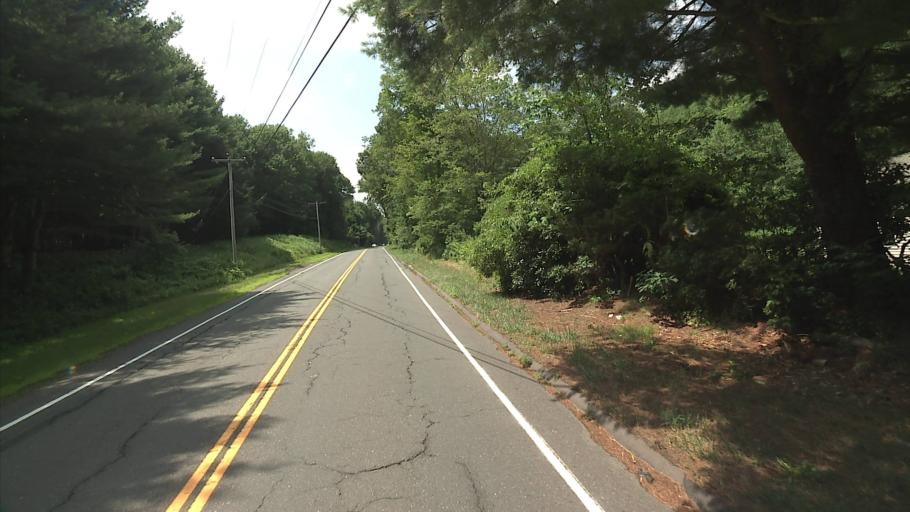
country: US
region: Connecticut
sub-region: Tolland County
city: Coventry Lake
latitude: 41.7924
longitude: -72.3560
